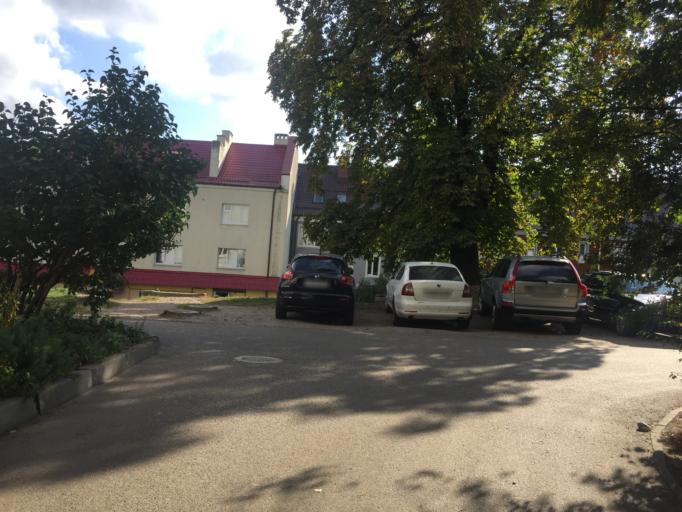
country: RU
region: Kaliningrad
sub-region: Gorod Kaliningrad
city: Kaliningrad
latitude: 54.6962
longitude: 20.5088
